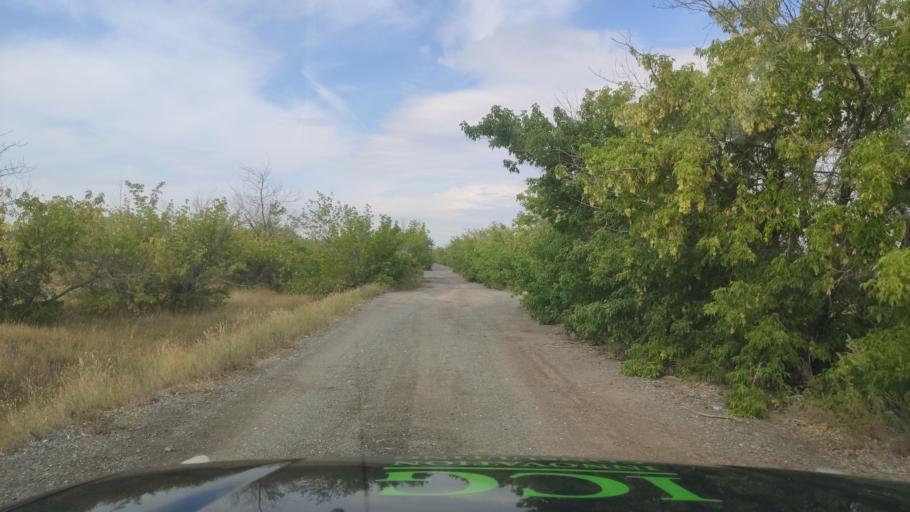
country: KZ
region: Pavlodar
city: Leninskiy
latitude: 52.4974
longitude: 76.8294
